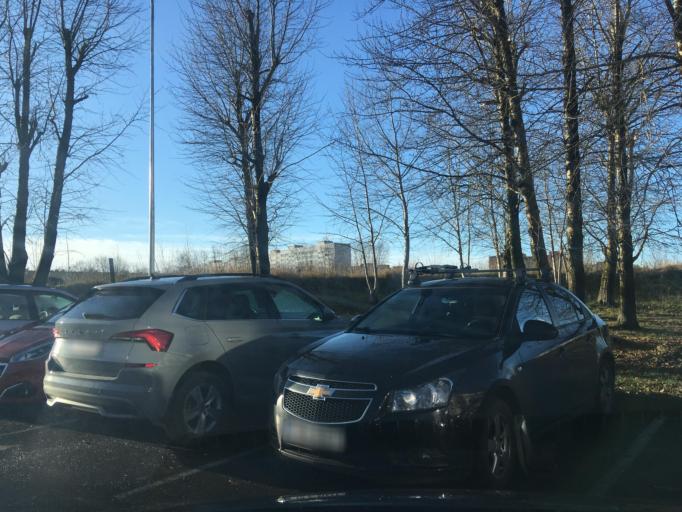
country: EE
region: Ida-Virumaa
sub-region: Narva linn
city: Narva
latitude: 59.3844
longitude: 28.1710
